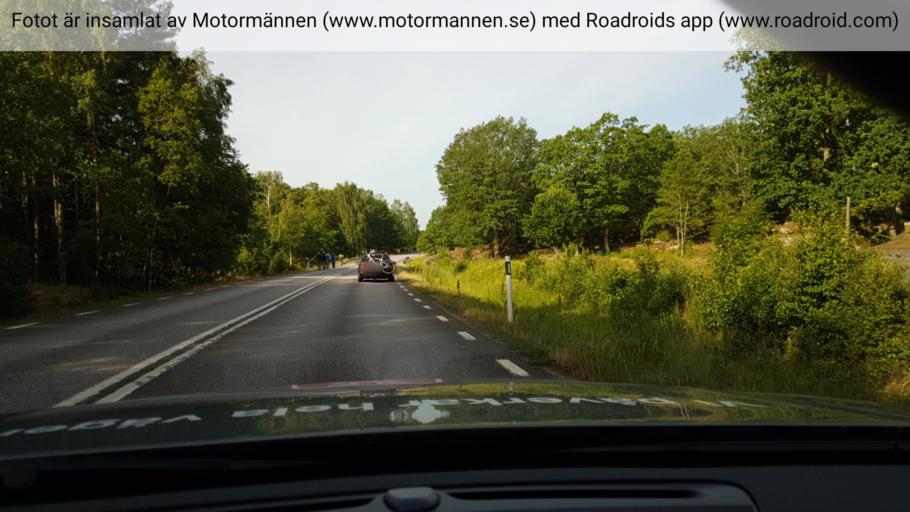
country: SE
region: Vaestra Goetaland
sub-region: Karlsborgs Kommun
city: Karlsborg
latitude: 58.6999
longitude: 14.7067
